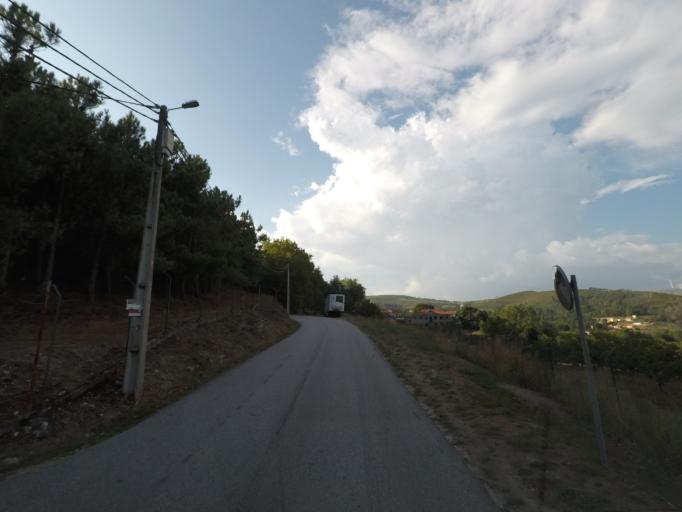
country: PT
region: Porto
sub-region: Baiao
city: Valadares
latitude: 41.1692
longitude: -7.9392
